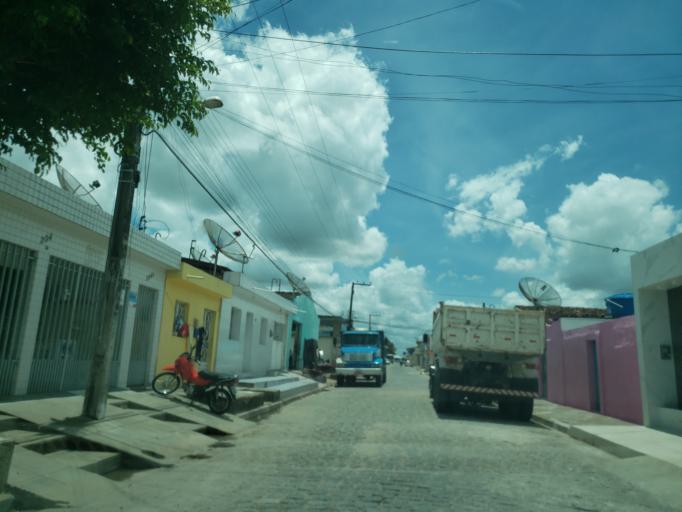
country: BR
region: Alagoas
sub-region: Uniao Dos Palmares
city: Uniao dos Palmares
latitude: -9.1635
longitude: -36.0224
